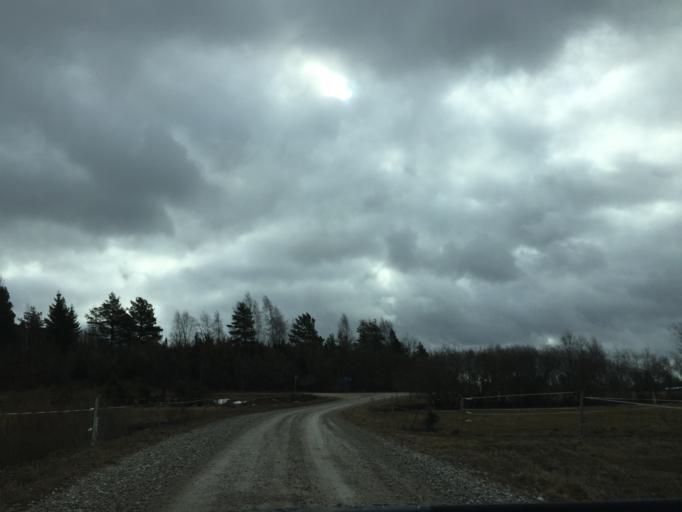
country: EE
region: Laeaene
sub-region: Haapsalu linn
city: Haapsalu
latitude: 58.6788
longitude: 23.5401
